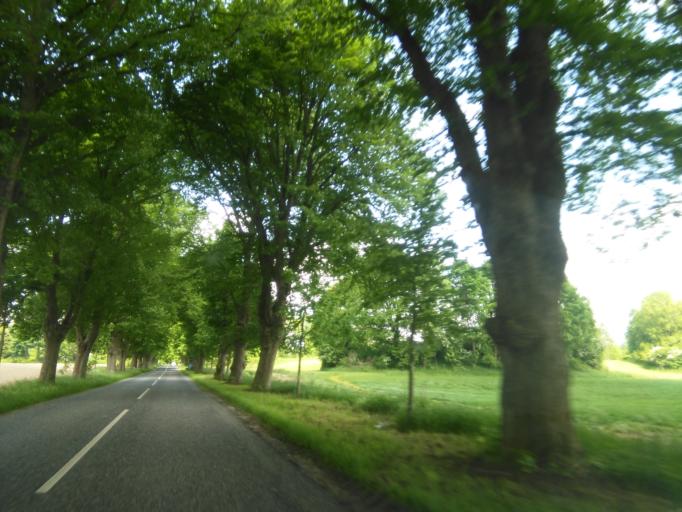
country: DK
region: Central Jutland
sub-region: Favrskov Kommune
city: Hammel
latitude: 56.2602
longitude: 9.8997
